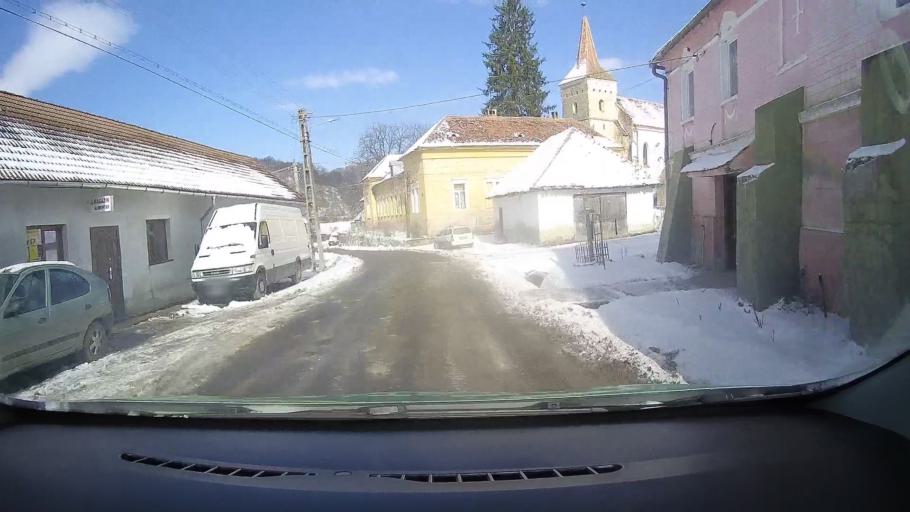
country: RO
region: Sibiu
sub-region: Comuna Mosna
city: Mosna
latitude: 46.0188
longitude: 24.4050
